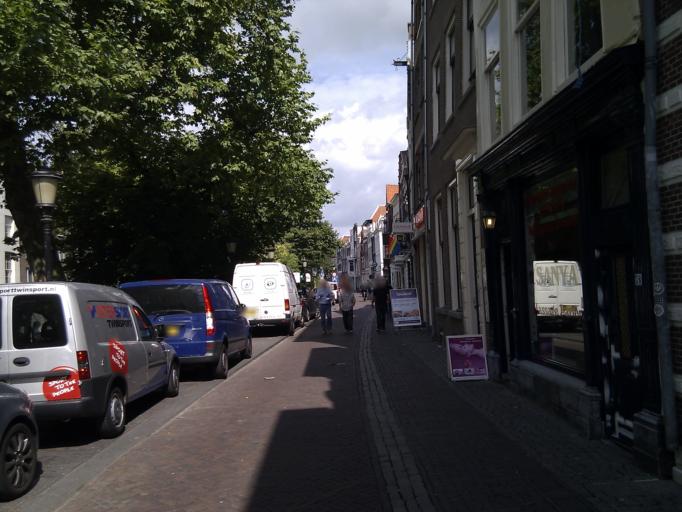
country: NL
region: Utrecht
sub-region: Gemeente Utrecht
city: Utrecht
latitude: 52.0941
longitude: 5.1168
